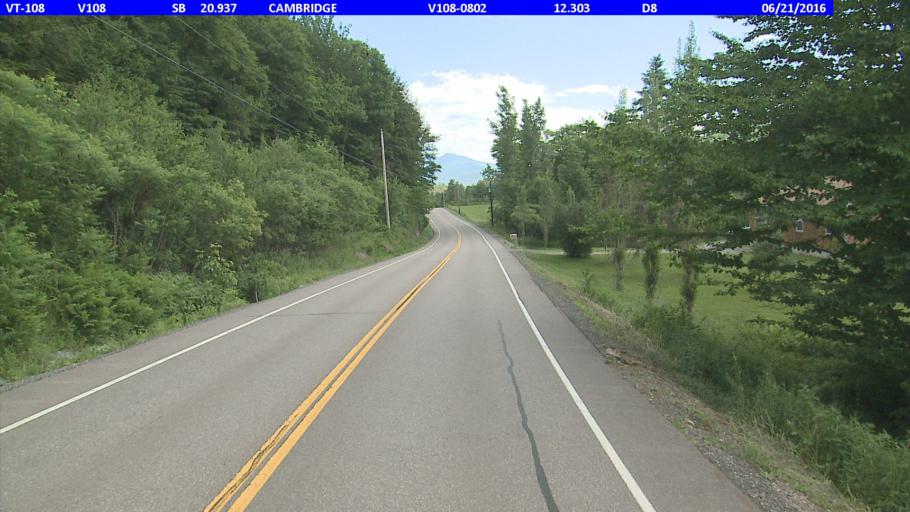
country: US
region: Vermont
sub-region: Lamoille County
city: Johnson
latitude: 44.6925
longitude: -72.8271
